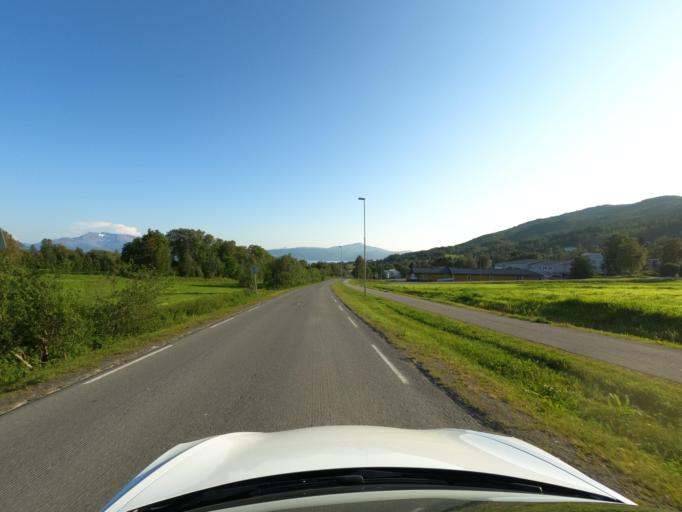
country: NO
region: Nordland
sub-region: Evenes
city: Randa
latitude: 68.4848
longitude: 16.8957
